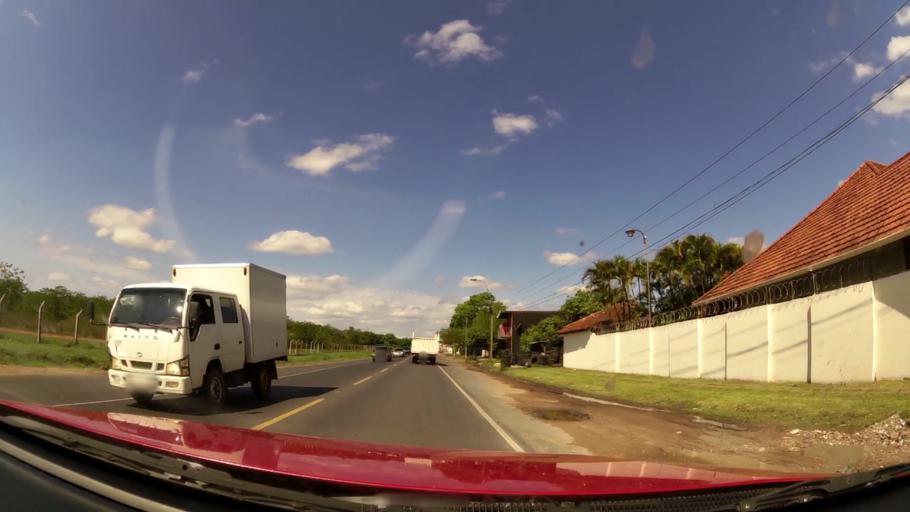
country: PY
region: Central
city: Fernando de la Mora
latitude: -25.2804
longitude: -57.5324
